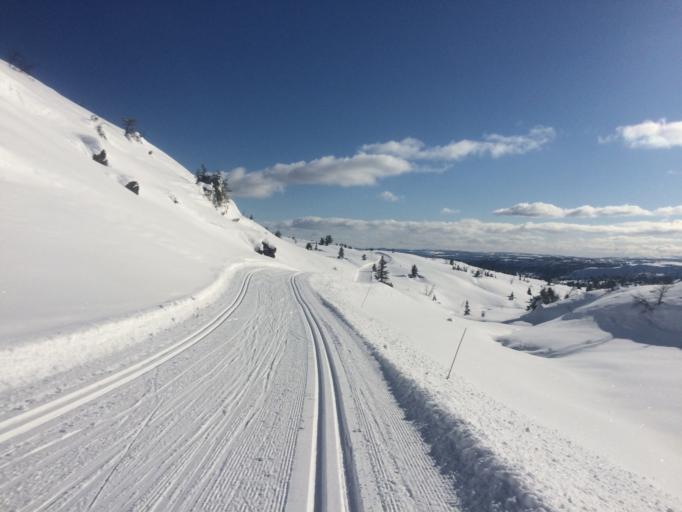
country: NO
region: Oppland
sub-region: Ringebu
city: Ringebu
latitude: 61.3757
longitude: 10.0594
